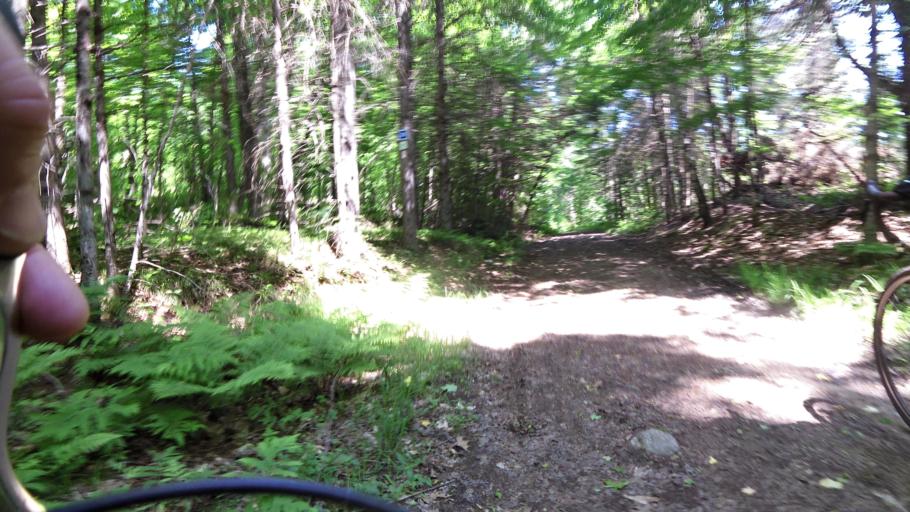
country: CA
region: Quebec
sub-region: Outaouais
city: Wakefield
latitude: 45.5579
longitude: -75.9035
